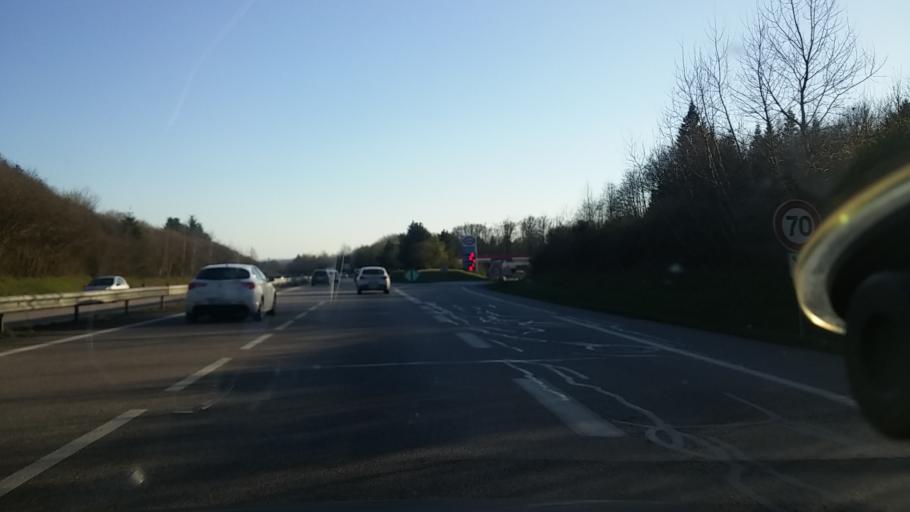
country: FR
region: Limousin
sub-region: Departement de la Haute-Vienne
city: Rilhac-Rancon
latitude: 45.9156
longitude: 1.2945
